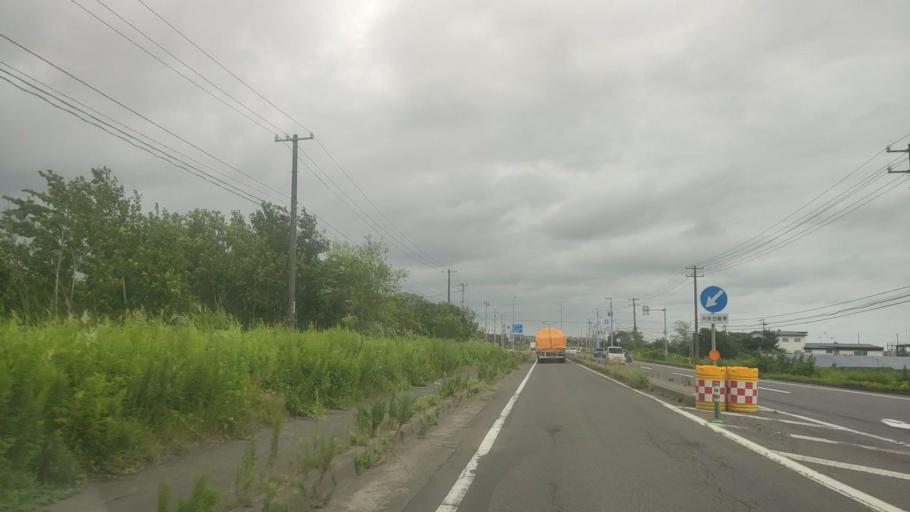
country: JP
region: Hokkaido
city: Shiraoi
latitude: 42.5273
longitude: 141.3200
